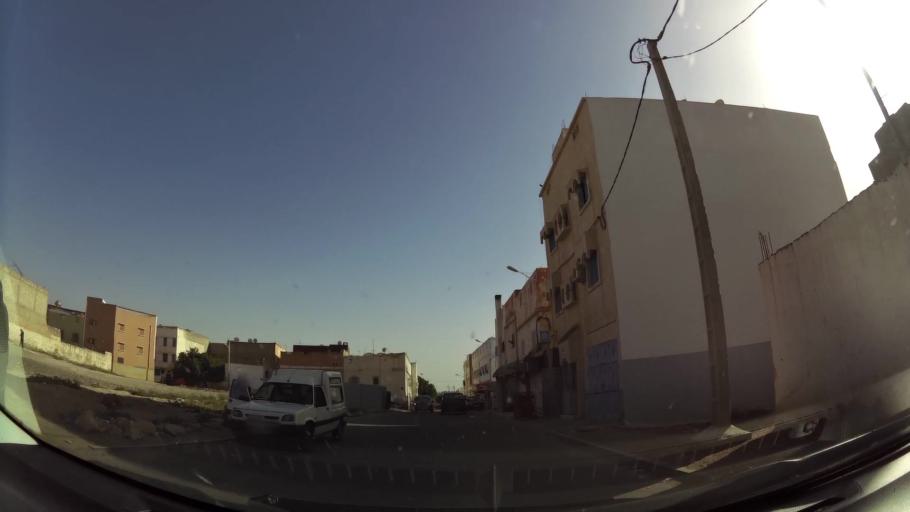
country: MA
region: Souss-Massa-Draa
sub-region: Inezgane-Ait Mellou
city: Inezgane
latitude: 30.3722
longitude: -9.5026
